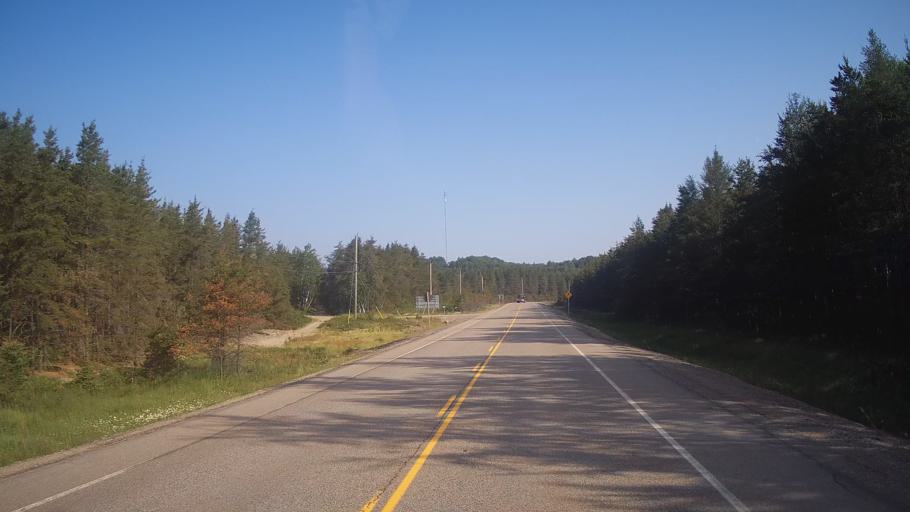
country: CA
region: Ontario
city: Rayside-Balfour
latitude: 46.7052
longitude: -81.5593
